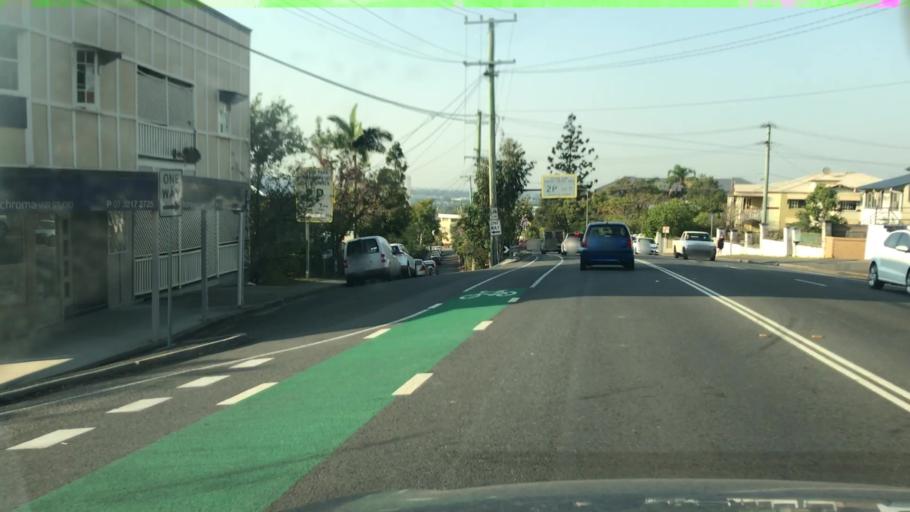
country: AU
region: Queensland
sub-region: Brisbane
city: South Brisbane
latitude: -27.4887
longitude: 153.0186
